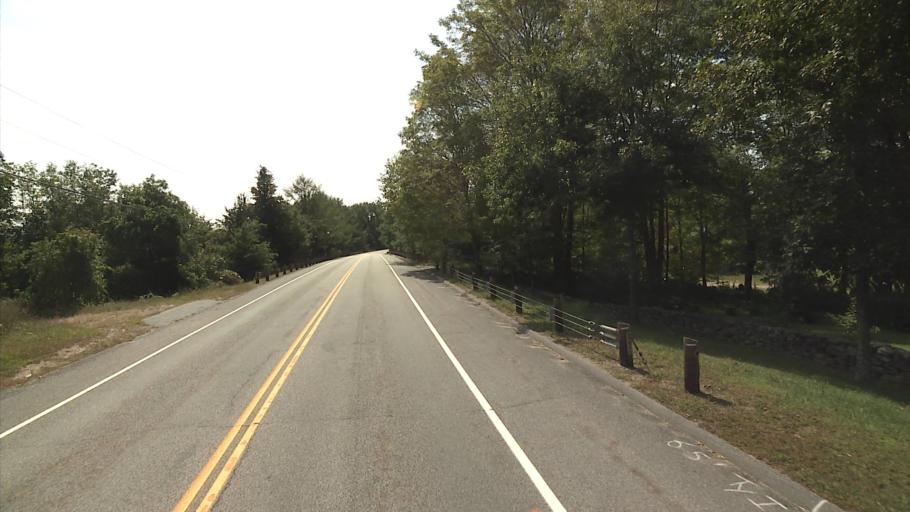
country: US
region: Connecticut
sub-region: Windham County
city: Wauregan
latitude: 41.7322
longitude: -71.9651
